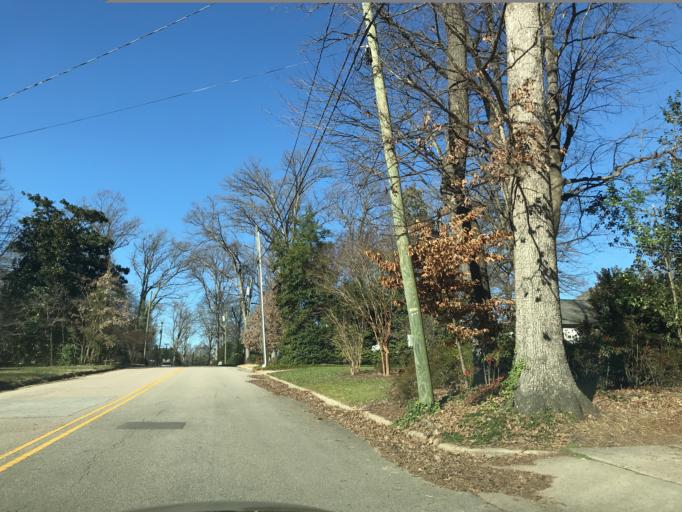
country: US
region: North Carolina
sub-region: Wake County
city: West Raleigh
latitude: 35.8101
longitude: -78.6438
